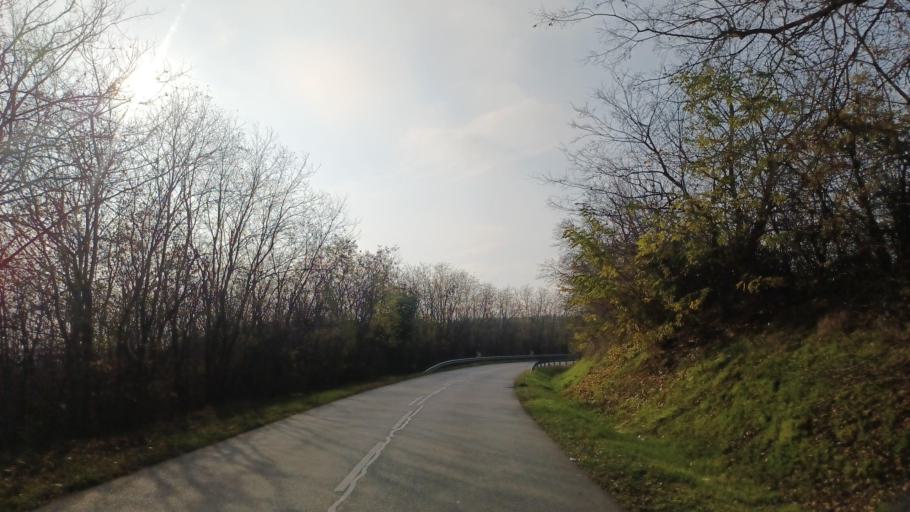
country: HU
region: Tolna
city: Tengelic
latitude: 46.5551
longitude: 18.7636
